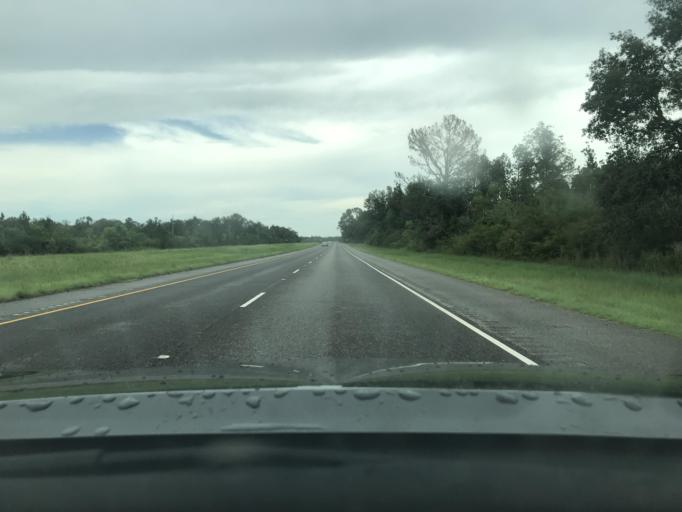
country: US
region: Louisiana
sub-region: Calcasieu Parish
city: Moss Bluff
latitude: 30.3878
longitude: -93.2186
